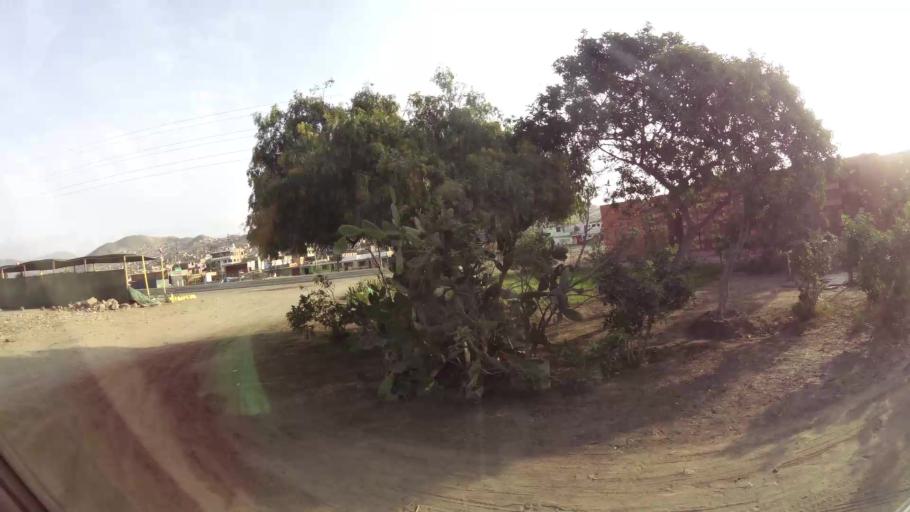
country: PE
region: Lima
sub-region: Lima
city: Santa Rosa
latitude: -11.7764
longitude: -77.1621
